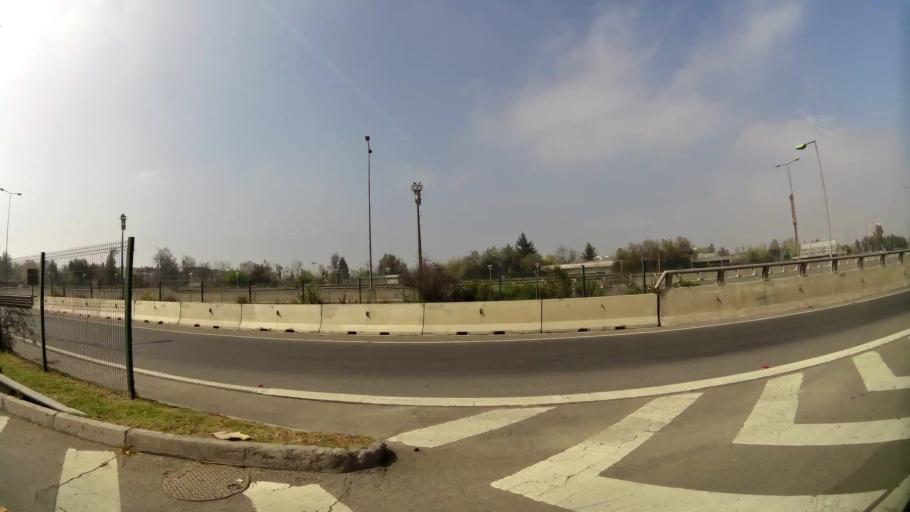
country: CL
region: Santiago Metropolitan
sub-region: Provincia de Santiago
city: Villa Presidente Frei, Nunoa, Santiago, Chile
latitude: -33.3864
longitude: -70.5953
